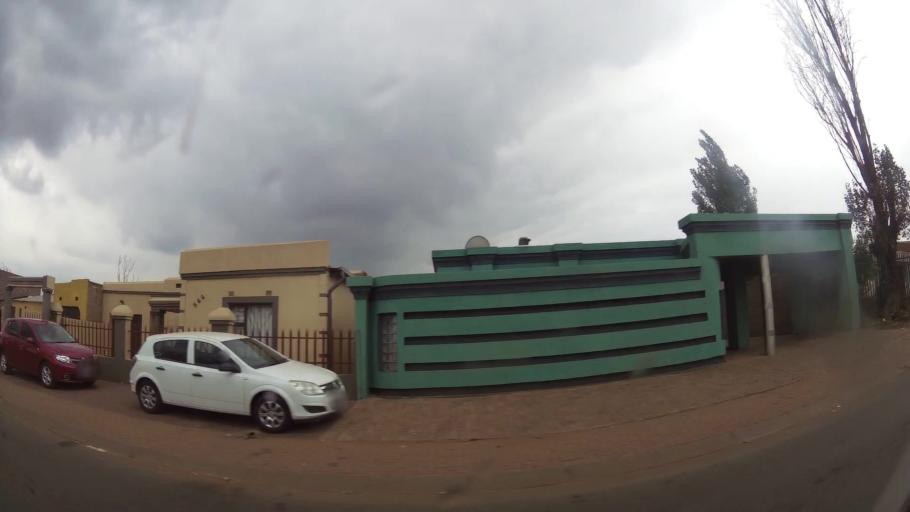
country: ZA
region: Gauteng
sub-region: Ekurhuleni Metropolitan Municipality
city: Germiston
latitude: -26.3251
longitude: 28.1541
